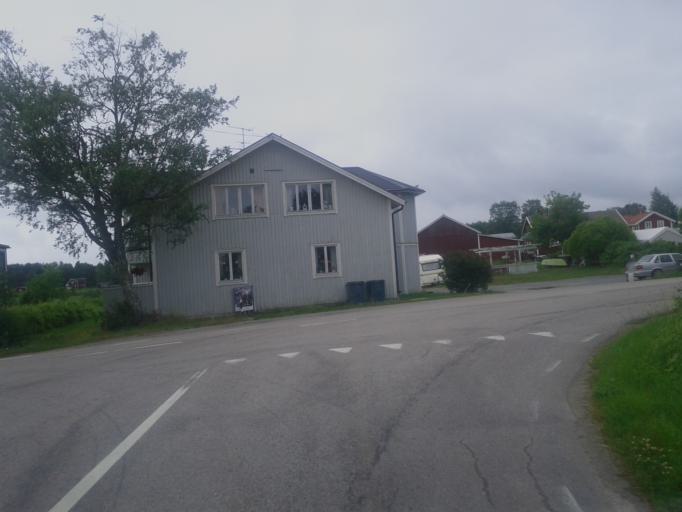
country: SE
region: Gaevleborg
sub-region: Nordanstigs Kommun
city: Bergsjoe
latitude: 61.9743
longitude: 17.2522
